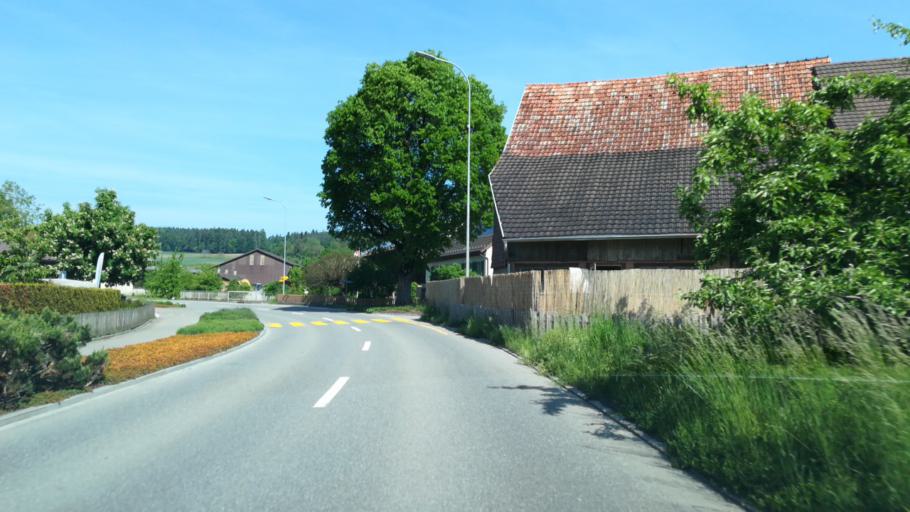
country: CH
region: Thurgau
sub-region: Frauenfeld District
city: Pfyn
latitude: 47.6008
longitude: 8.9508
